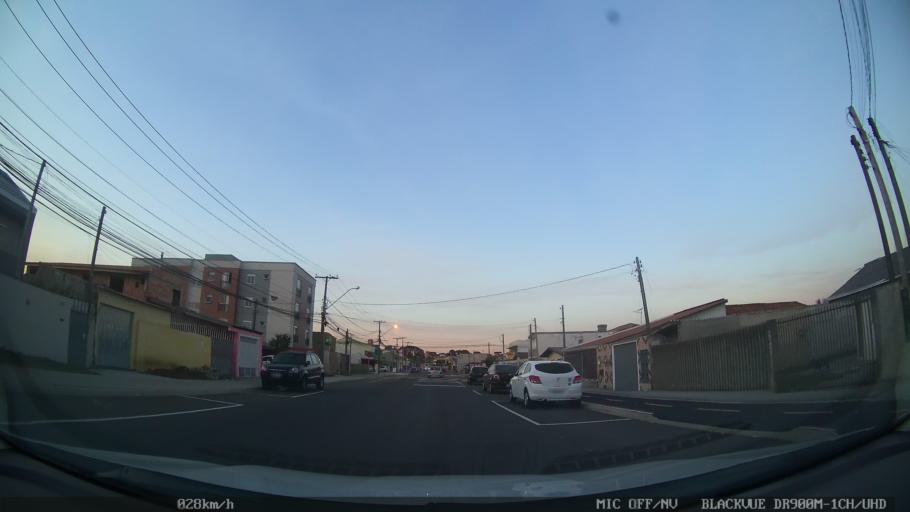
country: BR
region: Parana
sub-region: Pinhais
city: Pinhais
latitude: -25.4414
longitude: -49.1973
